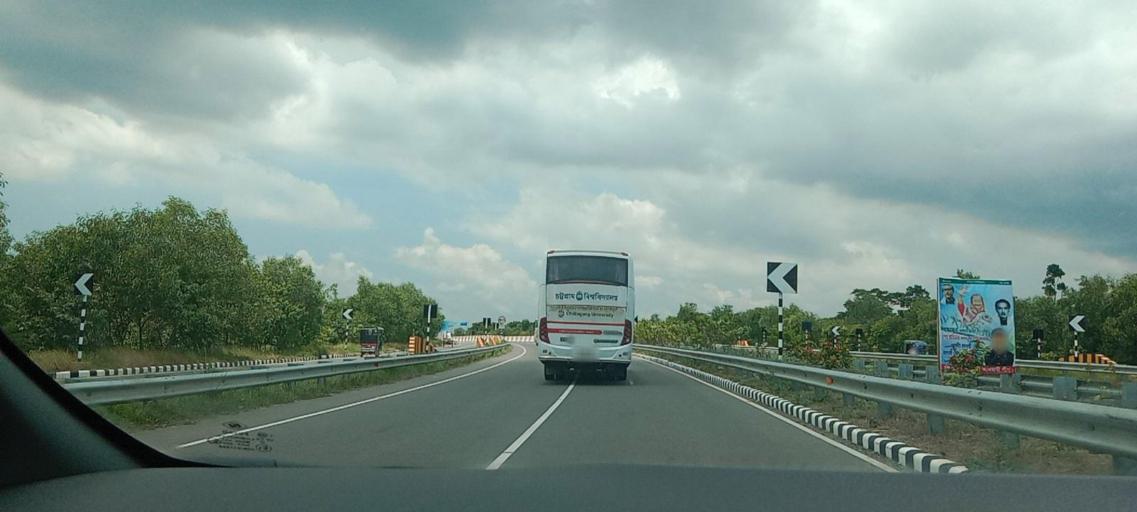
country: BD
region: Dhaka
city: Char Bhadrasan
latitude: 23.3813
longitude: 90.1241
